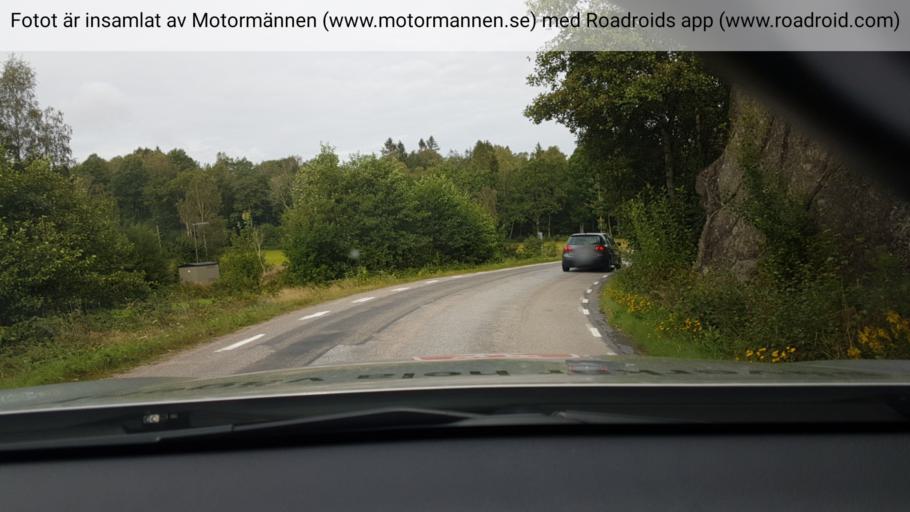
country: SE
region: Vaestra Goetaland
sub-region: Lysekils Kommun
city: Lysekil
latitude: 58.2490
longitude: 11.5514
